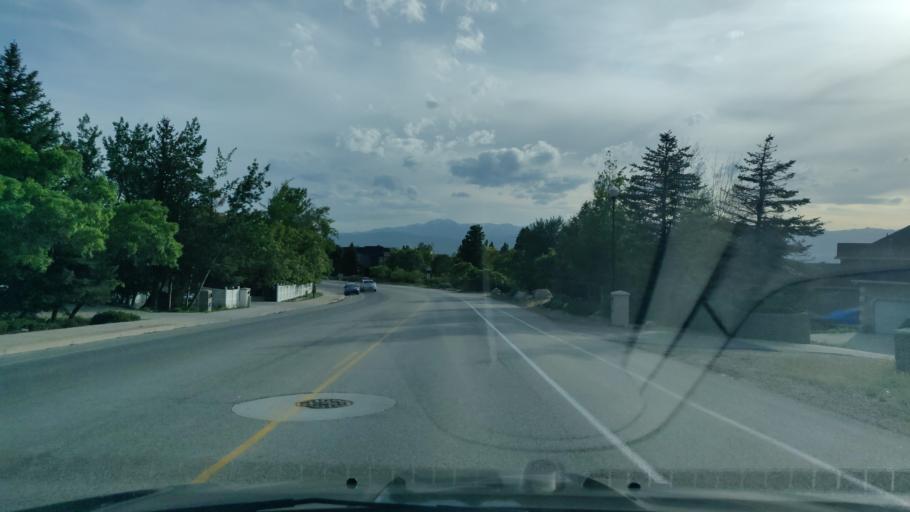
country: US
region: Utah
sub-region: Salt Lake County
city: Granite
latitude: 40.5439
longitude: -111.8114
